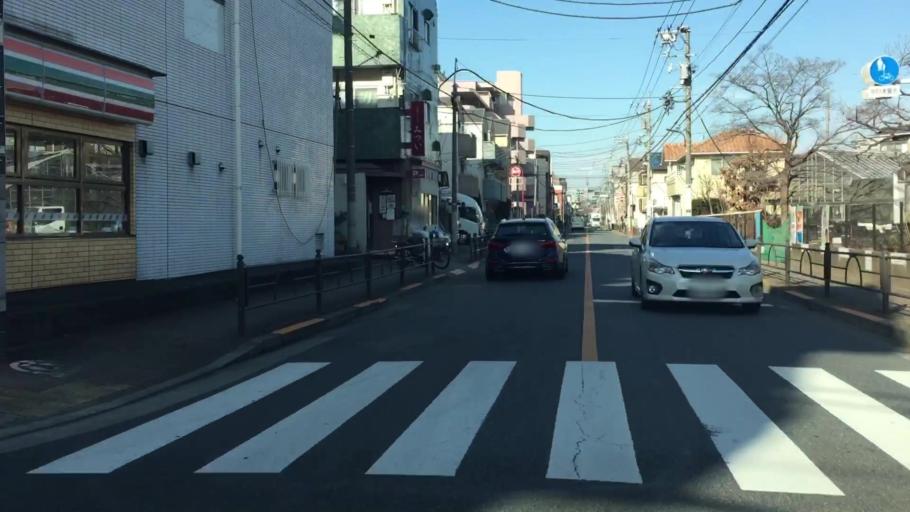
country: JP
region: Saitama
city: Wako
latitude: 35.7562
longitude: 139.6647
